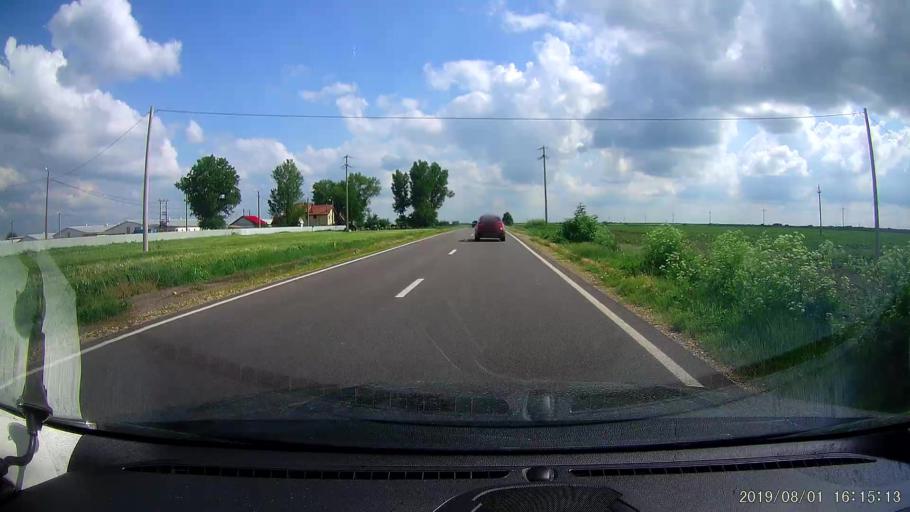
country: RO
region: Calarasi
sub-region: Comuna Stefan Voda
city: Stefan Voda
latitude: 44.3414
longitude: 27.3617
